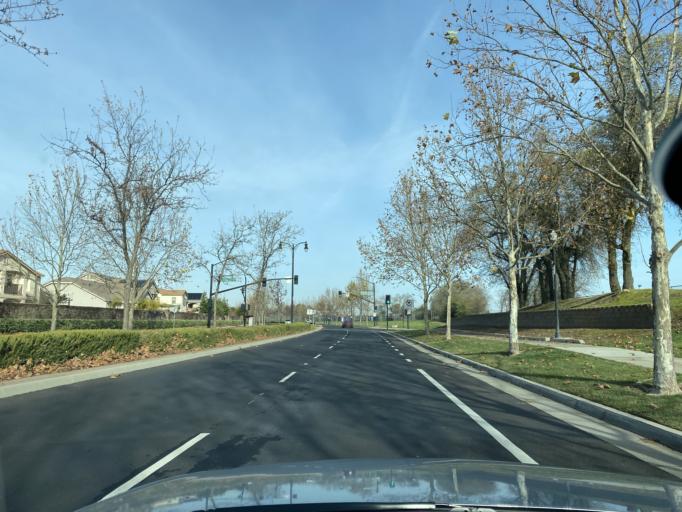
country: US
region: California
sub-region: Sacramento County
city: Elk Grove
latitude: 38.3966
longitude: -121.3994
